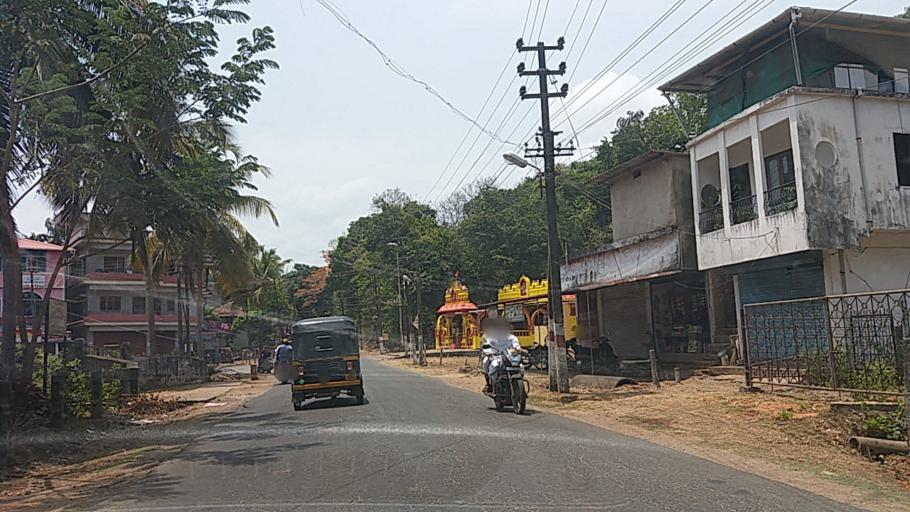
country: IN
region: Karnataka
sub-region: Uttar Kannada
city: Karwar
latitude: 14.8115
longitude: 74.1532
